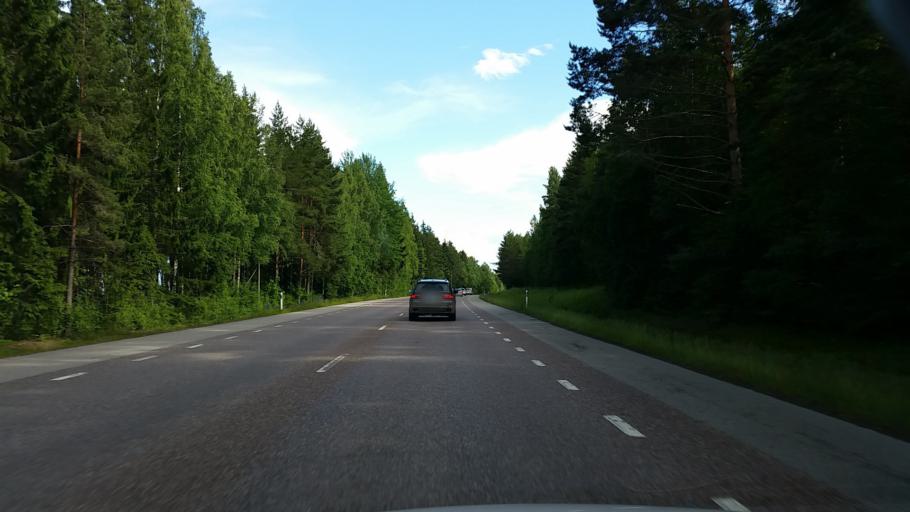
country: SE
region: Dalarna
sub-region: Smedjebackens Kommun
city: Smedjebacken
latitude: 60.0838
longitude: 15.5392
